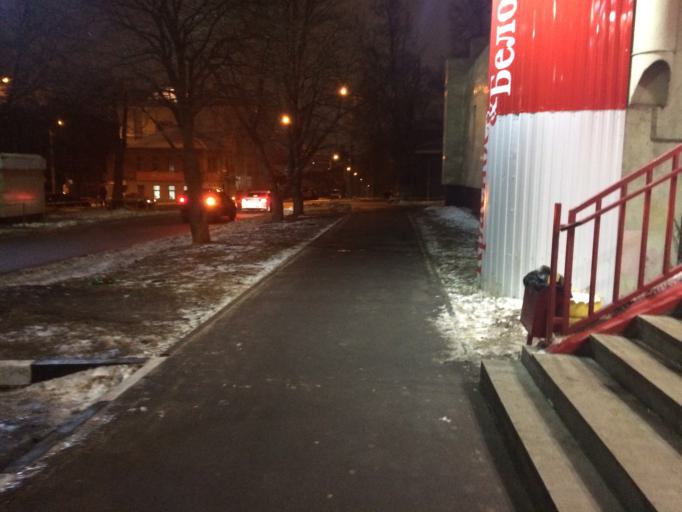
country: RU
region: Tula
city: Tula
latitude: 54.1880
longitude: 37.6016
